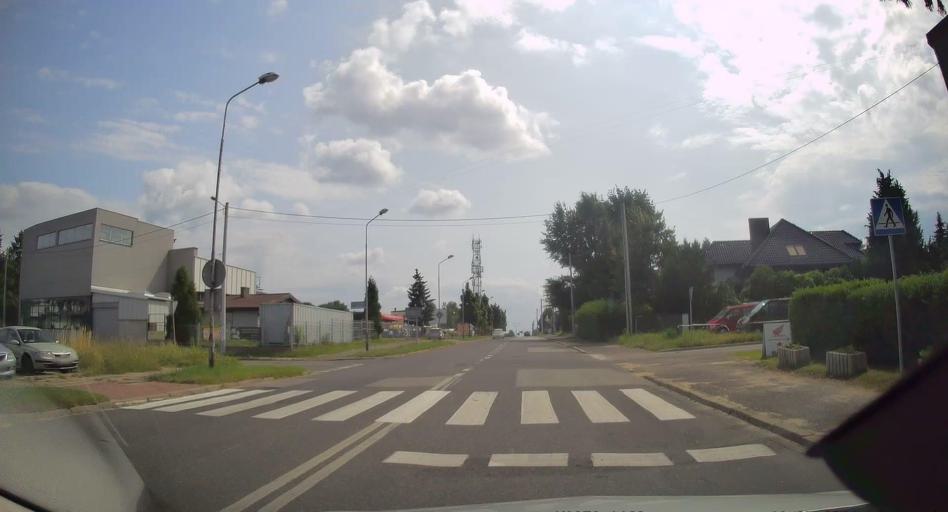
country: PL
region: Silesian Voivodeship
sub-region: Czestochowa
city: Czestochowa
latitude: 50.8170
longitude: 19.0854
